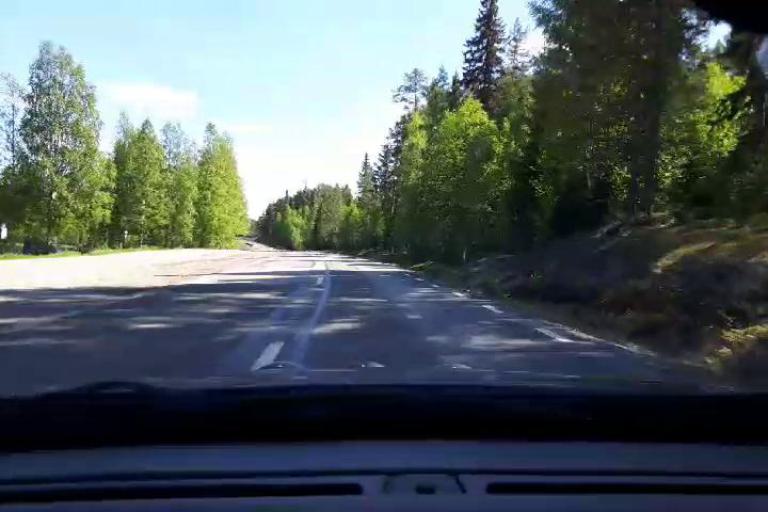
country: SE
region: Gaevleborg
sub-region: Ljusdals Kommun
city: Farila
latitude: 61.9755
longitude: 15.3329
